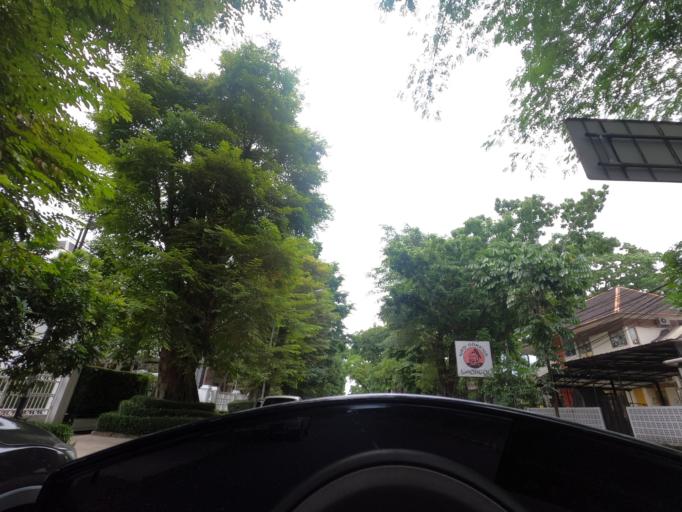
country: ID
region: West Java
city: Bandung
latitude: -6.8976
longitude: 107.6146
